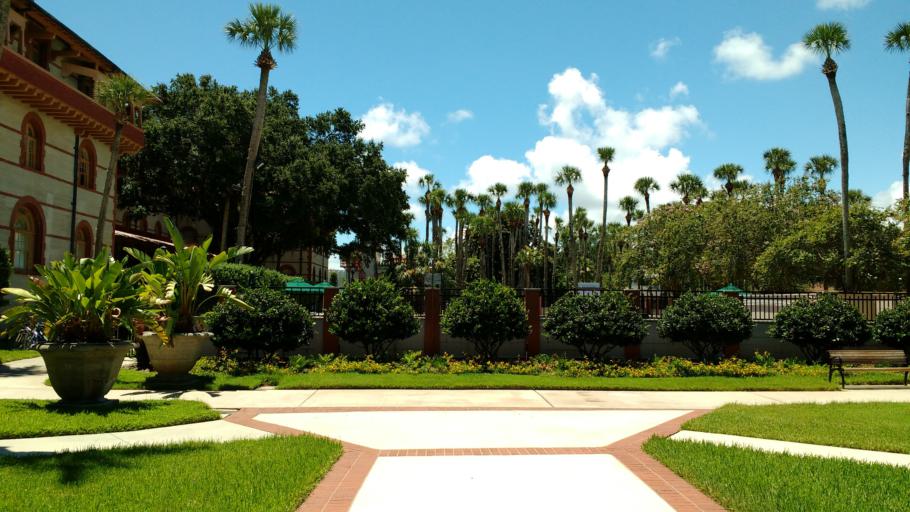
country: US
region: Florida
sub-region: Saint Johns County
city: Saint Augustine
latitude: 29.8929
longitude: -81.3156
